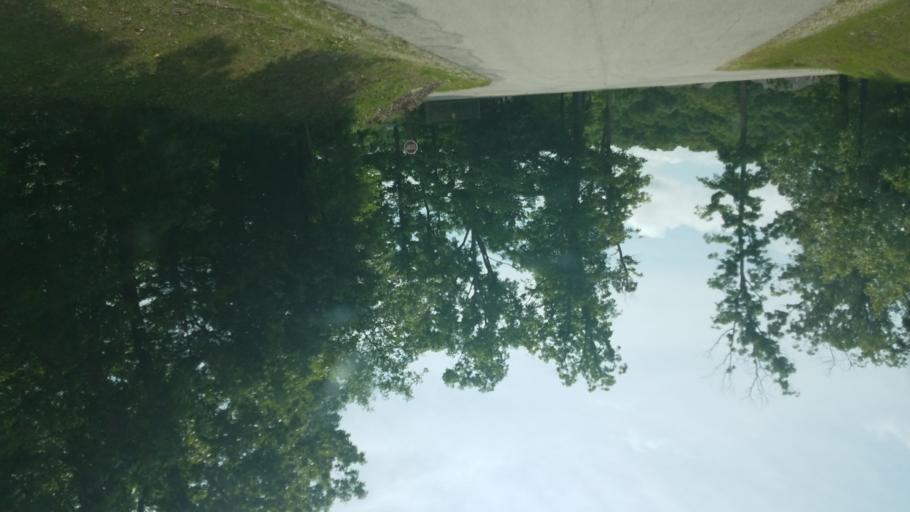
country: US
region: Missouri
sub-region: Camden County
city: Osage Beach
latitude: 38.1538
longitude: -92.6823
